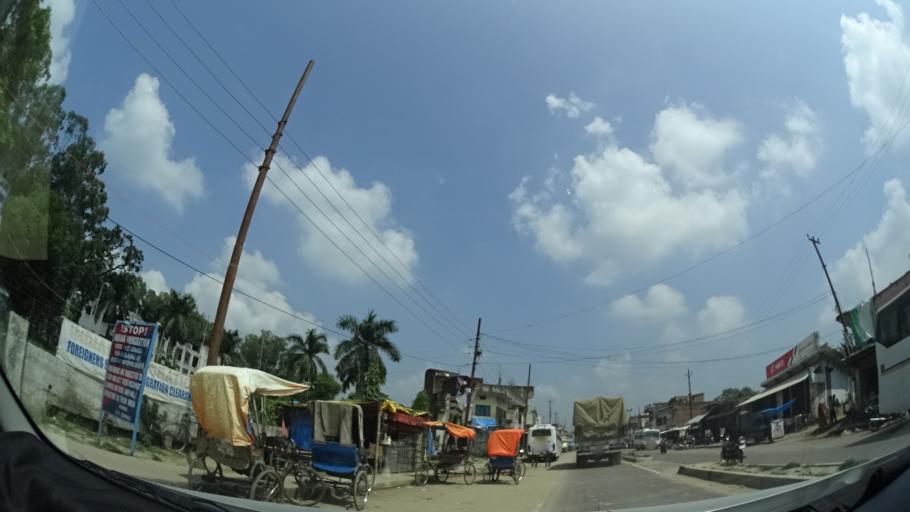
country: NP
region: Western Region
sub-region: Lumbini Zone
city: Bhairahawa
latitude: 27.4722
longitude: 83.4655
